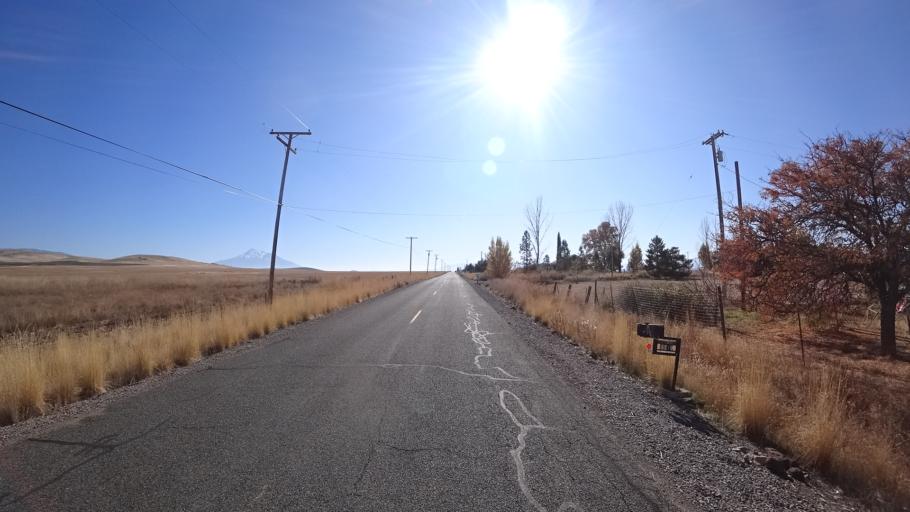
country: US
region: California
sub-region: Siskiyou County
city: Montague
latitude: 41.7535
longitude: -122.4571
